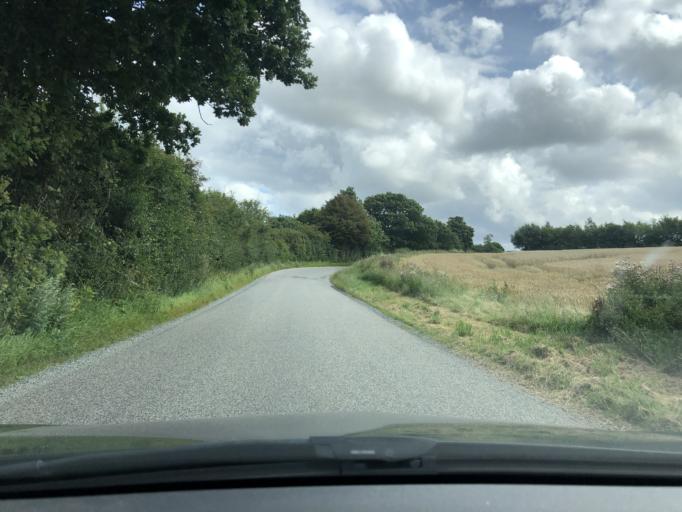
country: DK
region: South Denmark
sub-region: Vejle Kommune
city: Jelling
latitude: 55.6952
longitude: 9.4569
